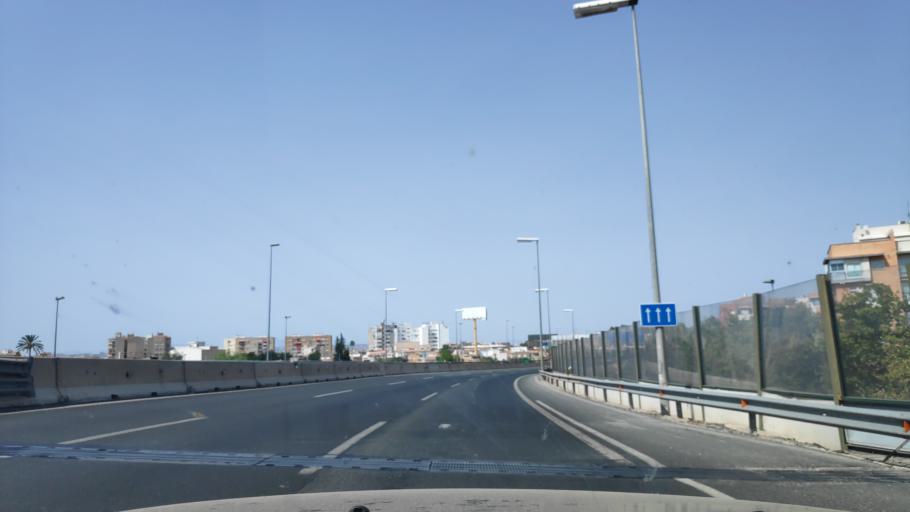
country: ES
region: Murcia
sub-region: Murcia
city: Murcia
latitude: 37.9708
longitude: -1.1383
